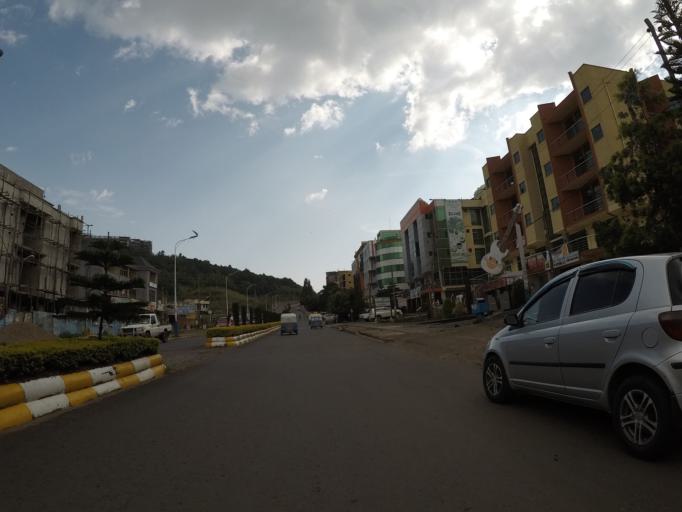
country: ET
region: Amhara
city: Gondar
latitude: 12.5937
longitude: 37.4471
